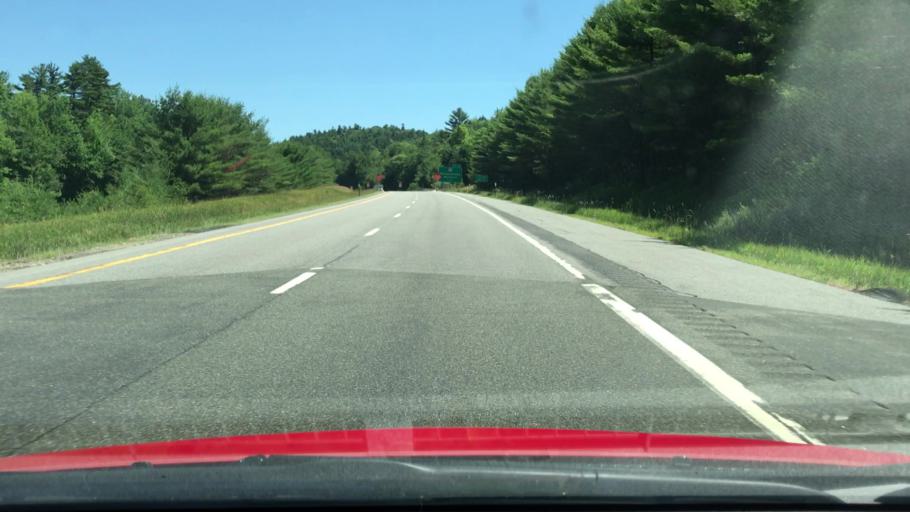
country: US
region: New York
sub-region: Essex County
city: Elizabethtown
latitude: 44.1972
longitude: -73.5243
